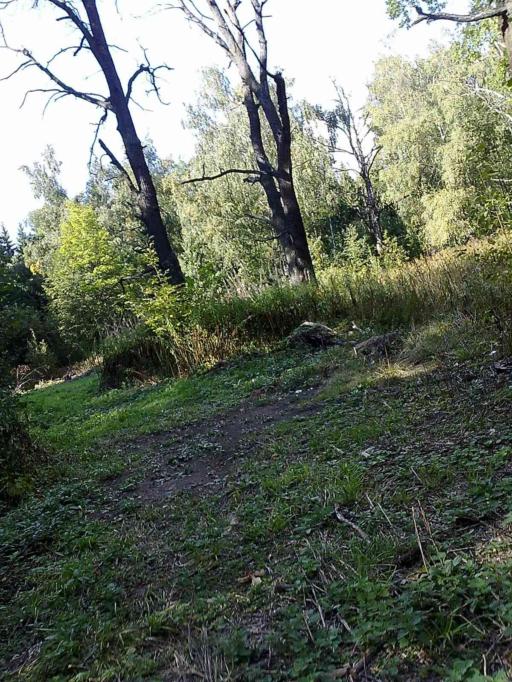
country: RU
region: Moskovskaya
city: Kokoshkino
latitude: 55.6178
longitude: 37.1722
